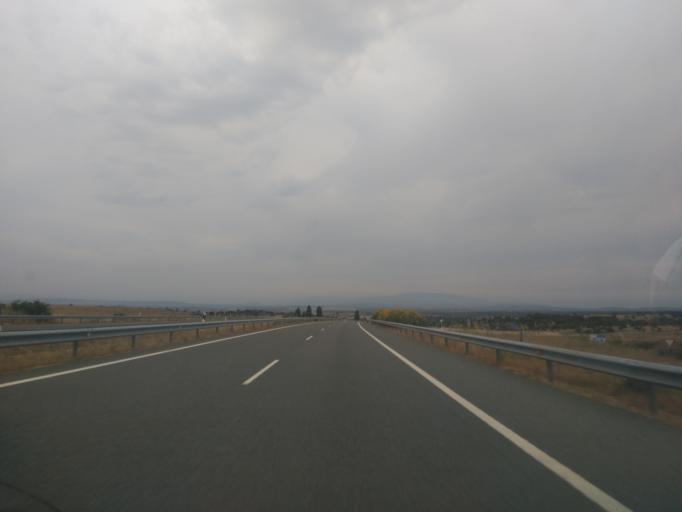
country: ES
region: Castille and Leon
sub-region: Provincia de Salamanca
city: Buenavista
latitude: 40.7700
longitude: -5.6278
